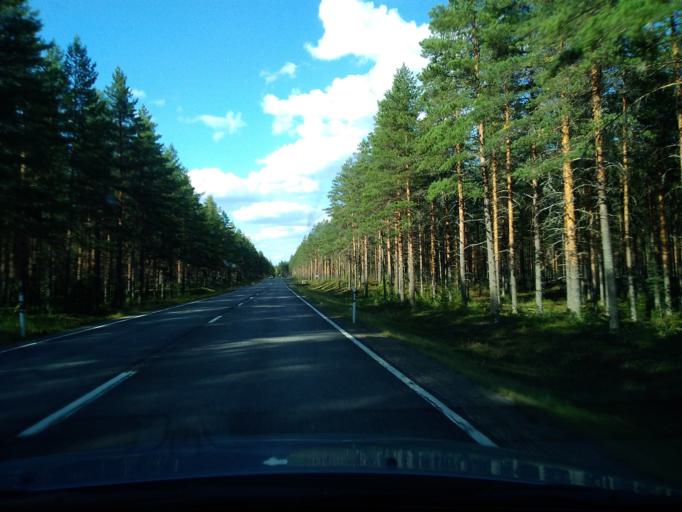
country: FI
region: Pirkanmaa
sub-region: Ylae-Pirkanmaa
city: Vilppula
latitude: 61.9411
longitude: 24.5414
